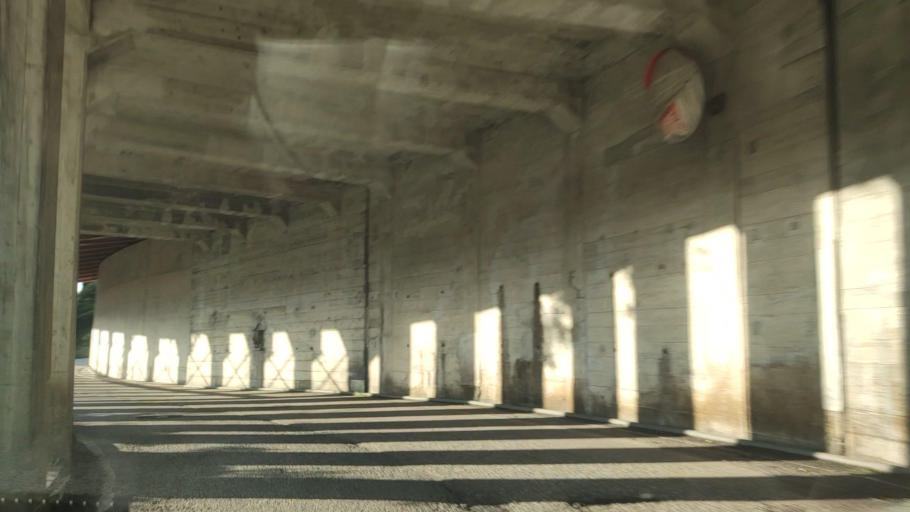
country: JP
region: Toyama
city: Yatsuomachi-higashikumisaka
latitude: 36.4926
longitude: 137.0251
